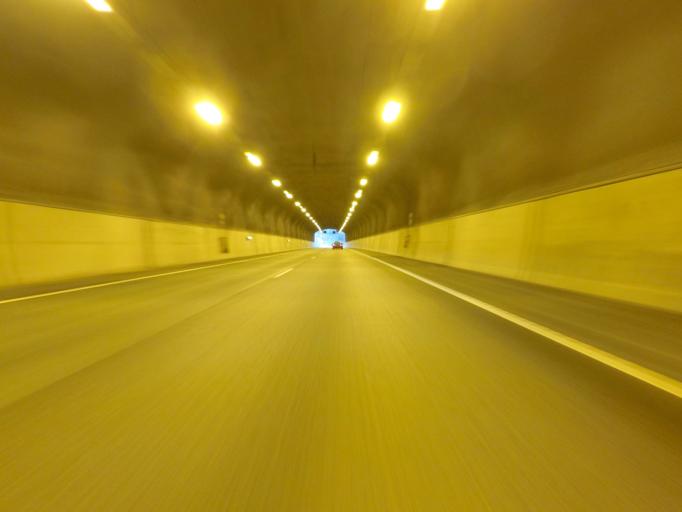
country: FI
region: Varsinais-Suomi
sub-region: Salo
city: Muurla
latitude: 60.3756
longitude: 23.3366
